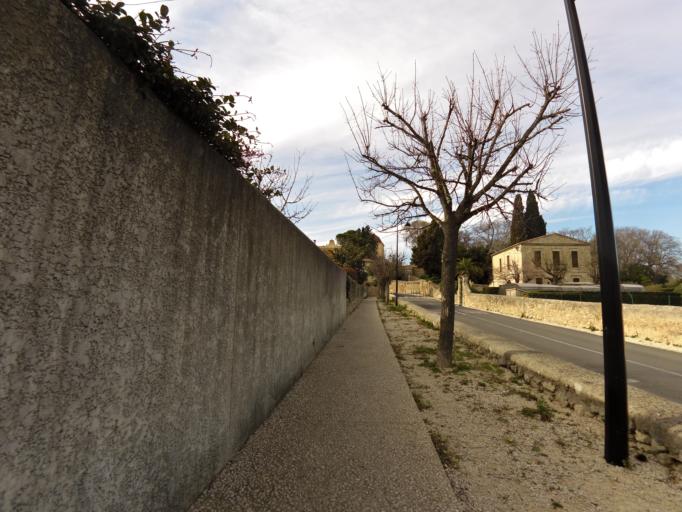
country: FR
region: Languedoc-Roussillon
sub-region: Departement de l'Herault
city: Castries
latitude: 43.6762
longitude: 3.9890
